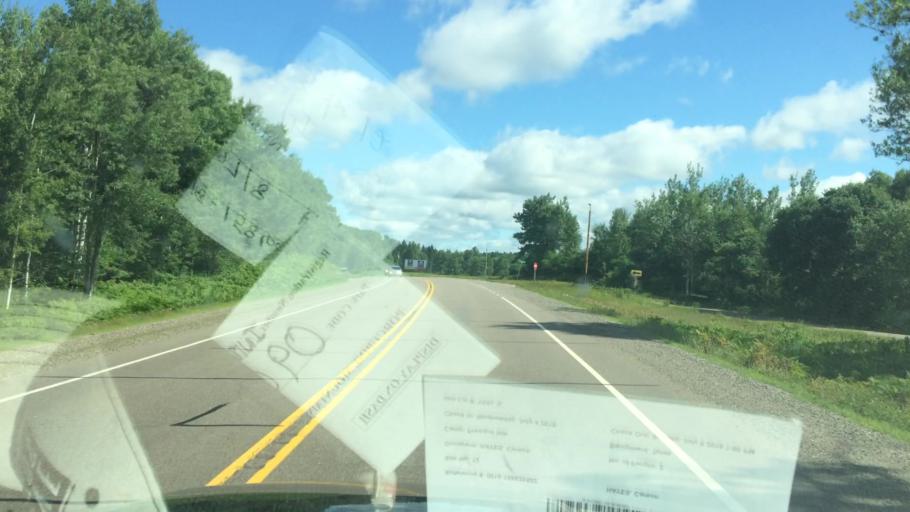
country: US
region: Wisconsin
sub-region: Oneida County
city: Rhinelander
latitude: 45.5753
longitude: -89.5700
